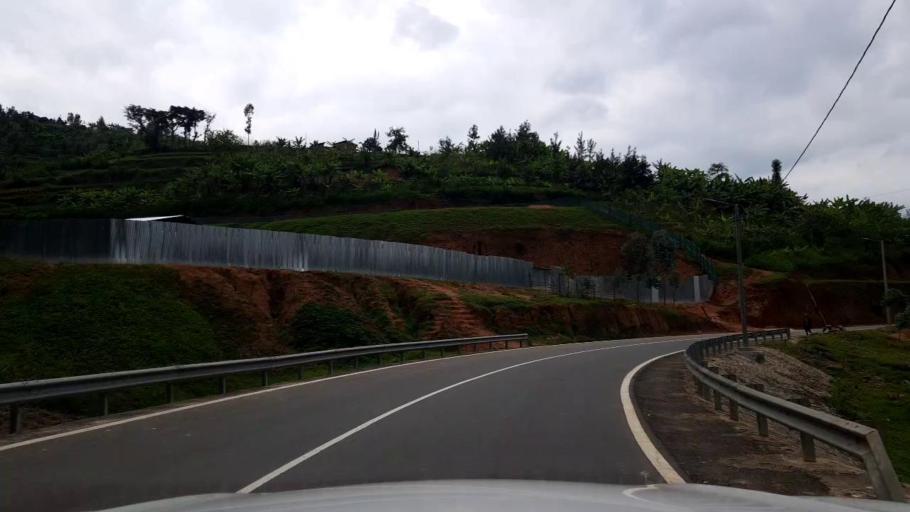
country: RW
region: Western Province
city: Kibuye
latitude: -1.9260
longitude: 29.3742
